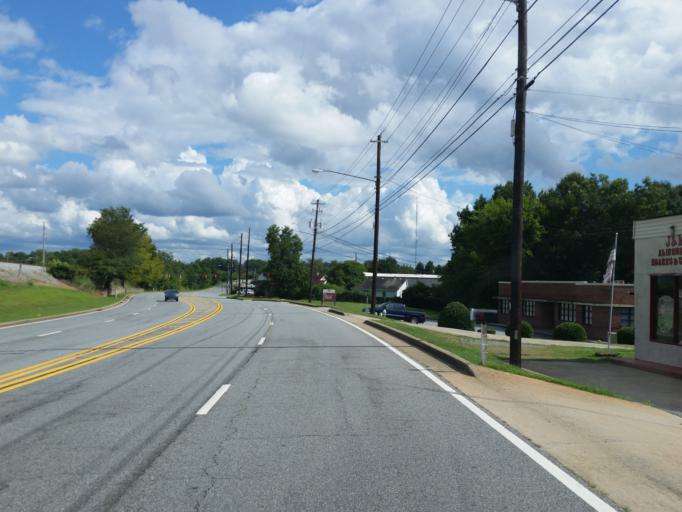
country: US
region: Georgia
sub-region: Cobb County
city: Marietta
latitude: 33.9397
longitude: -84.5448
